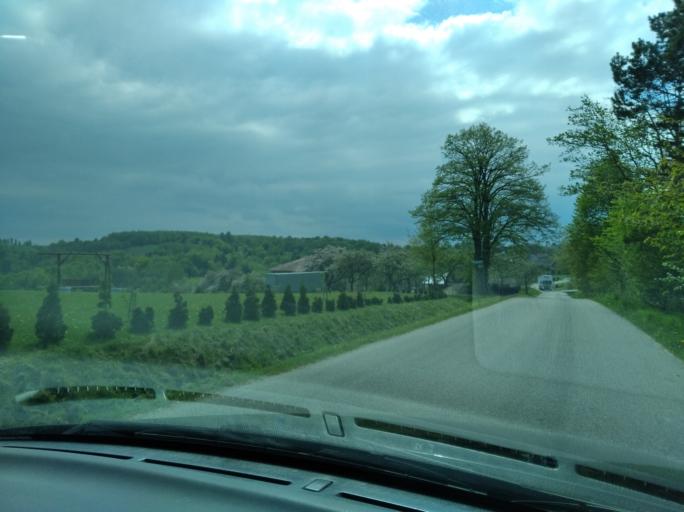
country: PL
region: Subcarpathian Voivodeship
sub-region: Powiat ropczycko-sedziszowski
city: Wielopole Skrzynskie
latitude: 49.9139
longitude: 21.6072
